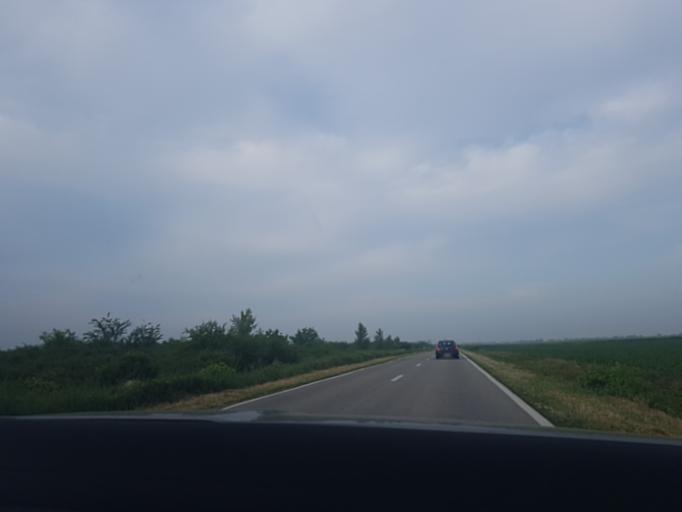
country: RO
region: Timis
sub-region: Comuna Peciu Nou
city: Peciu Nou
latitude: 45.6237
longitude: 21.0882
